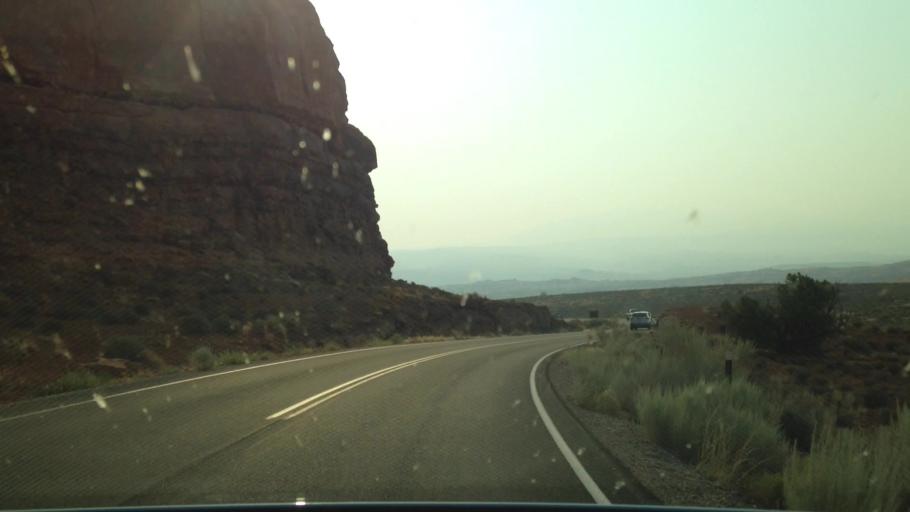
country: US
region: Utah
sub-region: Grand County
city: Moab
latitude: 38.6244
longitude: -109.5991
